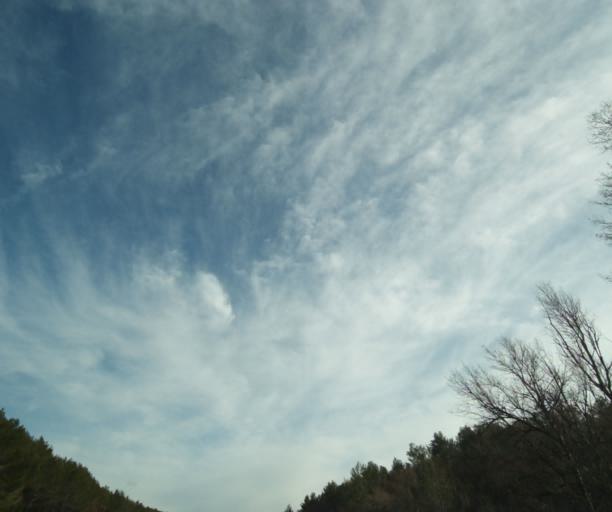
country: FR
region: Provence-Alpes-Cote d'Azur
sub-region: Departement du Var
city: Camps-la-Source
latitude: 43.4159
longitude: 6.1283
